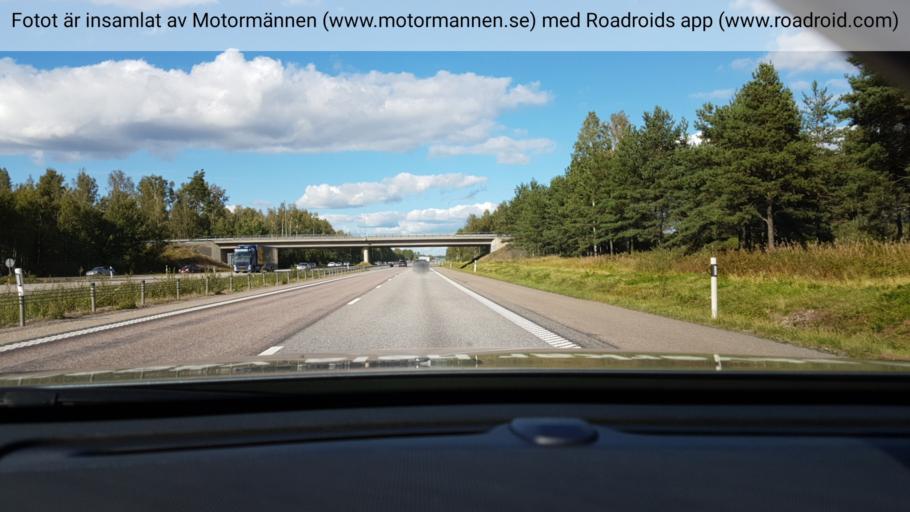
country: SE
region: OErebro
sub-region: Kumla Kommun
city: Kumla
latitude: 59.2128
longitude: 15.1313
